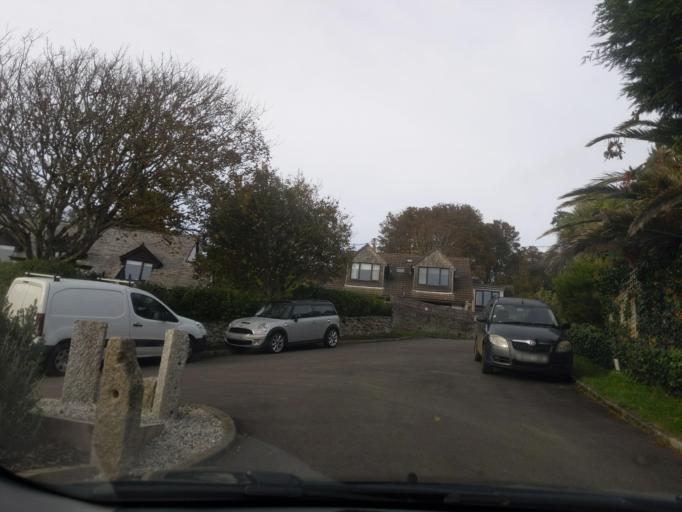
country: GB
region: England
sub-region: Cornwall
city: Looe
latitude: 50.3610
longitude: -4.4395
